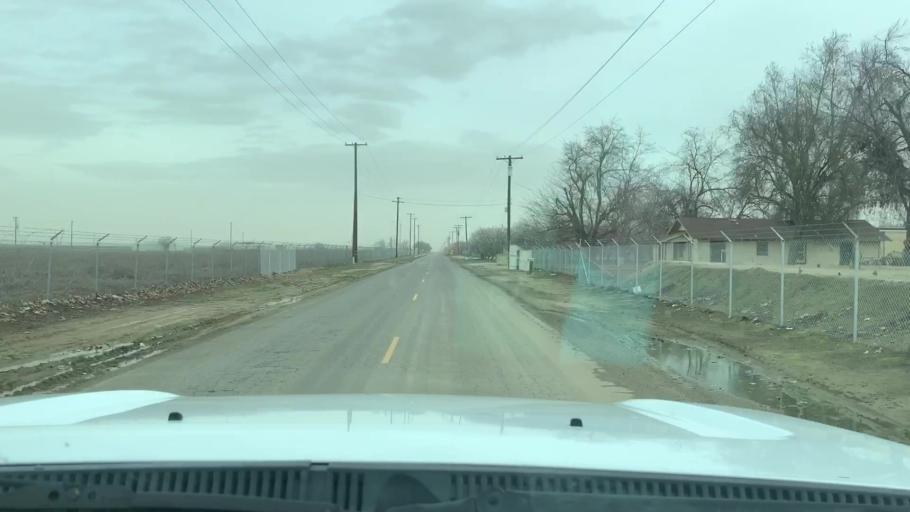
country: US
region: California
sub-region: Kern County
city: Shafter
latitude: 35.5292
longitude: -119.2653
